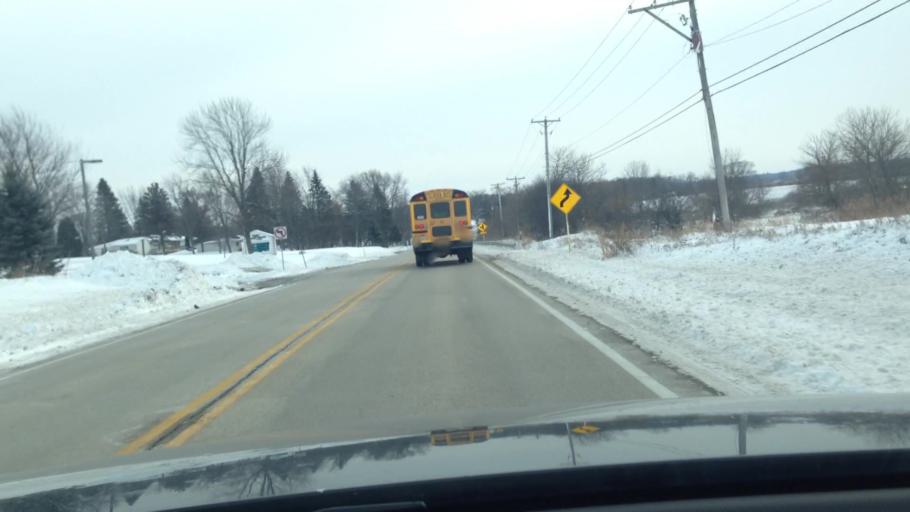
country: US
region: Illinois
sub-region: McHenry County
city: Woodstock
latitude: 42.3566
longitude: -88.4431
